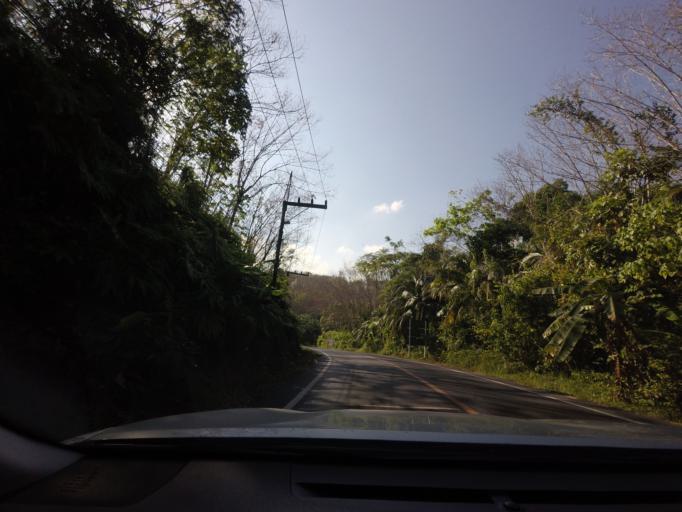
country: TH
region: Phangnga
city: Takua Thung
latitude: 8.2535
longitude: 98.3776
